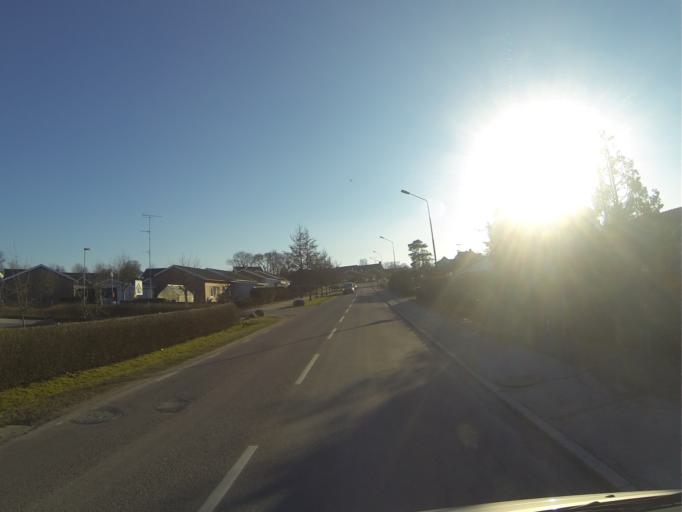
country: SE
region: Skane
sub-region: Hoors Kommun
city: Loberod
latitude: 55.7780
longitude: 13.5181
